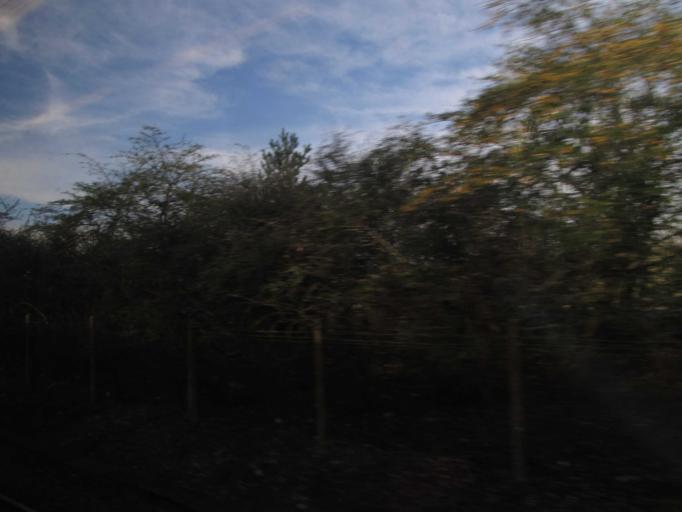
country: GB
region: England
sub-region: Surrey
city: Shalford
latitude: 51.2120
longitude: -0.5826
